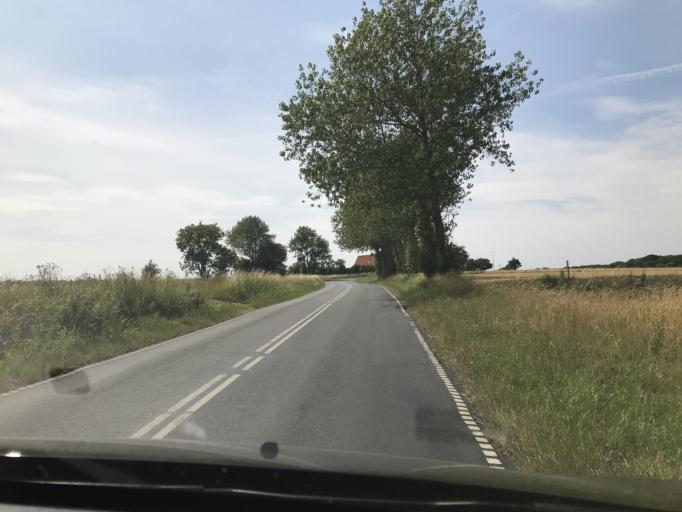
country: DK
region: South Denmark
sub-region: AEro Kommune
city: AEroskobing
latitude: 54.8659
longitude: 10.3759
